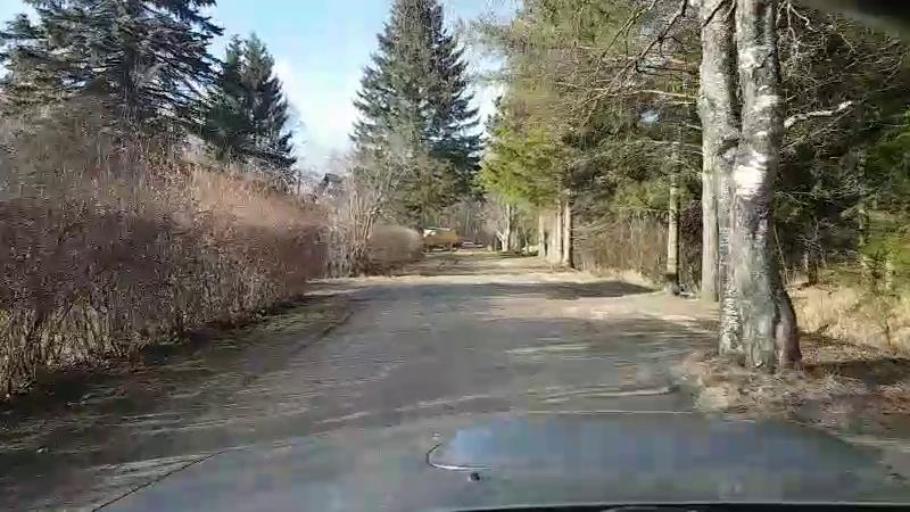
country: EE
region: Jaervamaa
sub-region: Paide linn
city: Paide
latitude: 58.8892
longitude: 25.5314
